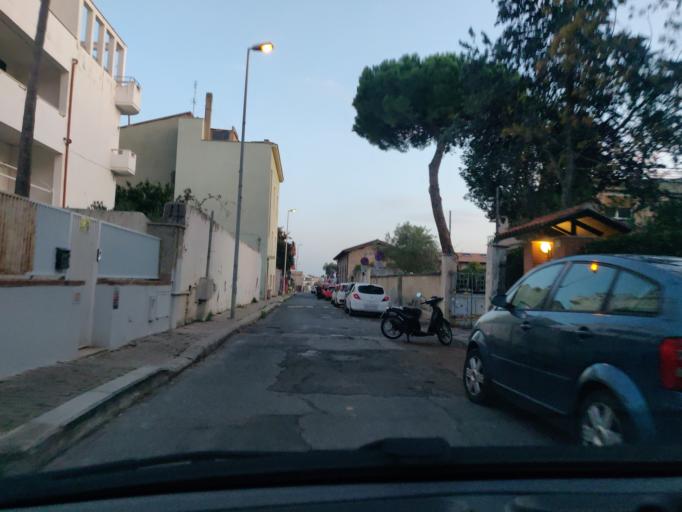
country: IT
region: Latium
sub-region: Citta metropolitana di Roma Capitale
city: Civitavecchia
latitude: 42.0830
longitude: 11.8039
